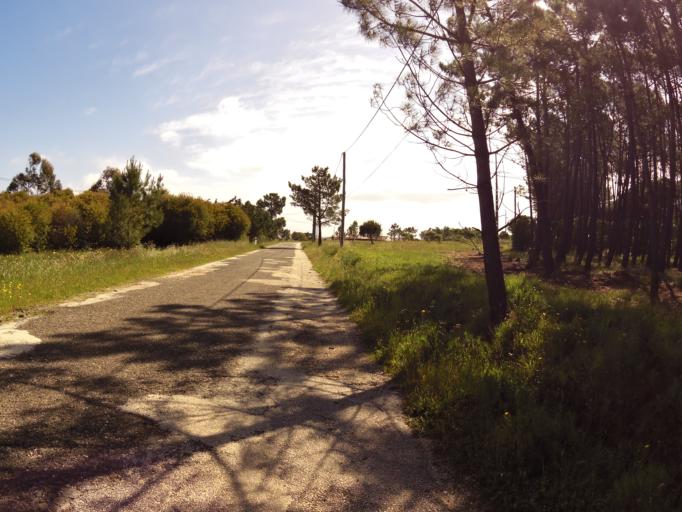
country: PT
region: Faro
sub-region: Aljezur
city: Aljezur
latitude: 37.3400
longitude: -8.8049
